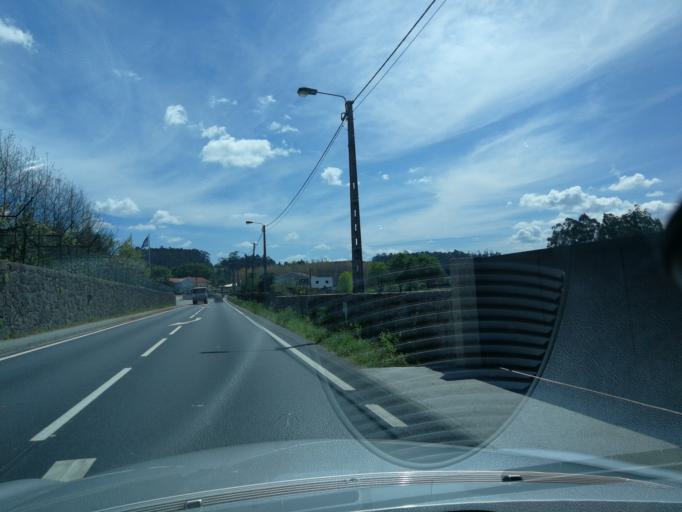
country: PT
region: Braga
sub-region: Vila Nova de Famalicao
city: Calendario
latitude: 41.4304
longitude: -8.5370
